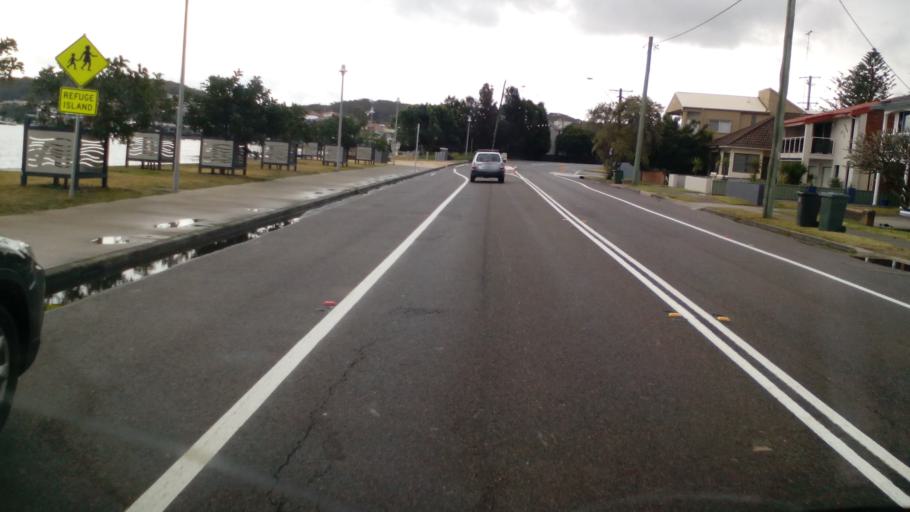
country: AU
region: New South Wales
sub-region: Lake Macquarie Shire
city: Belmont
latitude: -33.0335
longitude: 151.6562
